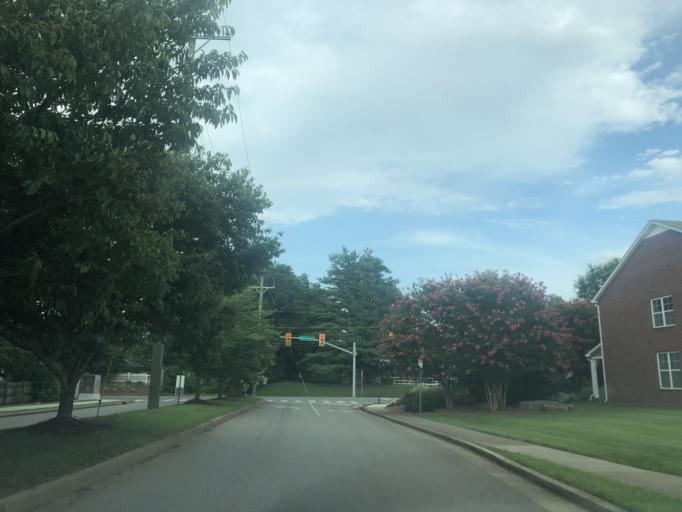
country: US
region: Tennessee
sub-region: Davidson County
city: Lakewood
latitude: 36.1699
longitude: -86.6158
